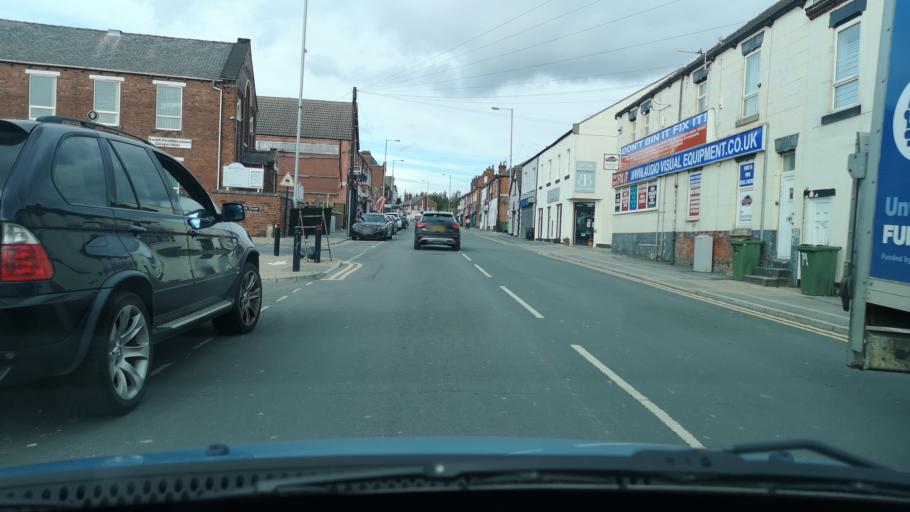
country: GB
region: England
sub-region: City and Borough of Wakefield
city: Featherstone
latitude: 53.6771
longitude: -1.3587
